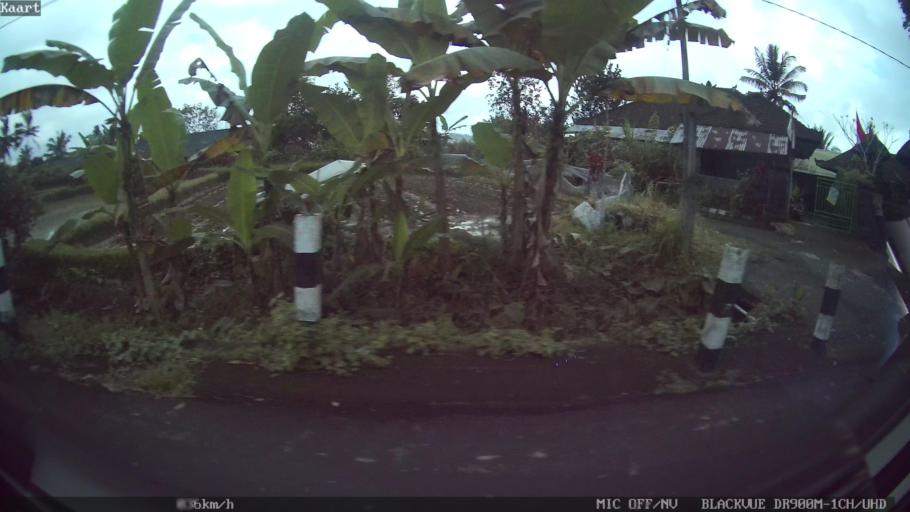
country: ID
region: Bali
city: Peneng
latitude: -8.3603
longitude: 115.1851
